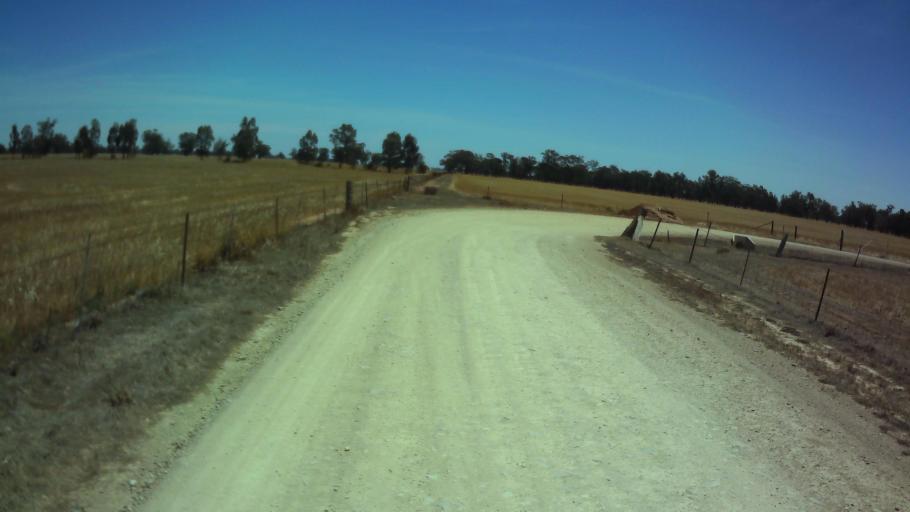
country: AU
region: New South Wales
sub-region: Weddin
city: Grenfell
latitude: -34.0543
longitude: 147.7668
